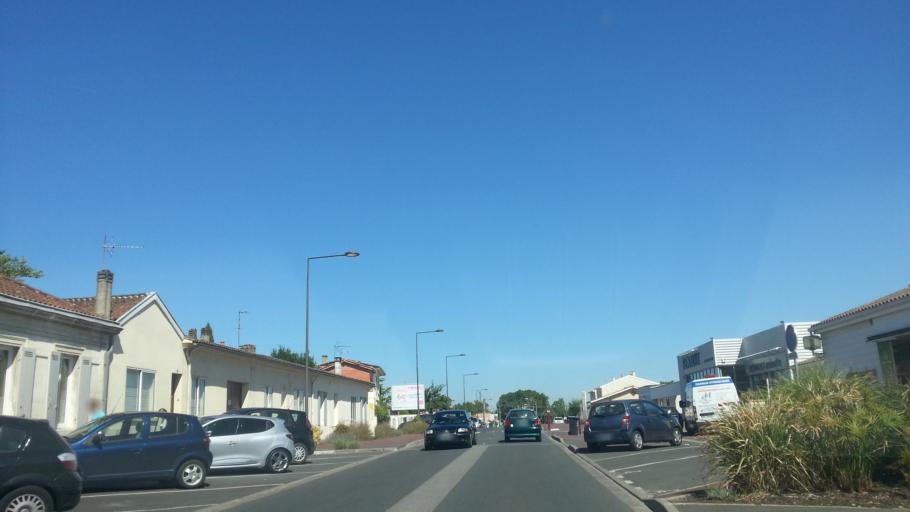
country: FR
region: Aquitaine
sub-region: Departement de la Gironde
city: Cadaujac
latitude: 44.7518
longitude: -0.5490
